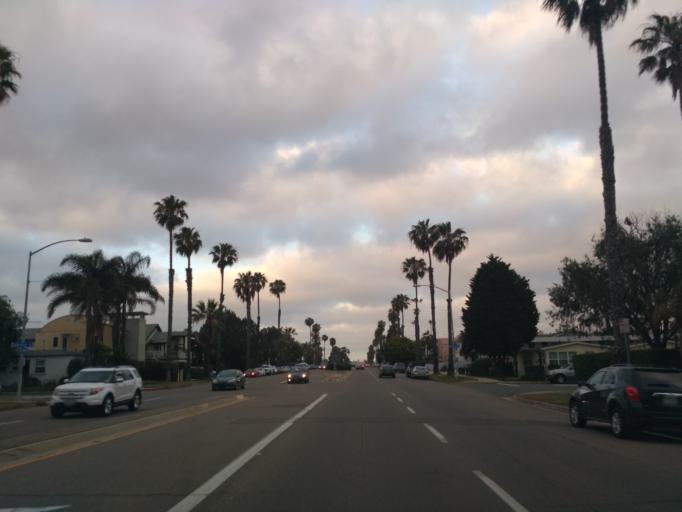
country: US
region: California
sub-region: San Diego County
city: La Jolla
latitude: 32.7969
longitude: -117.2446
